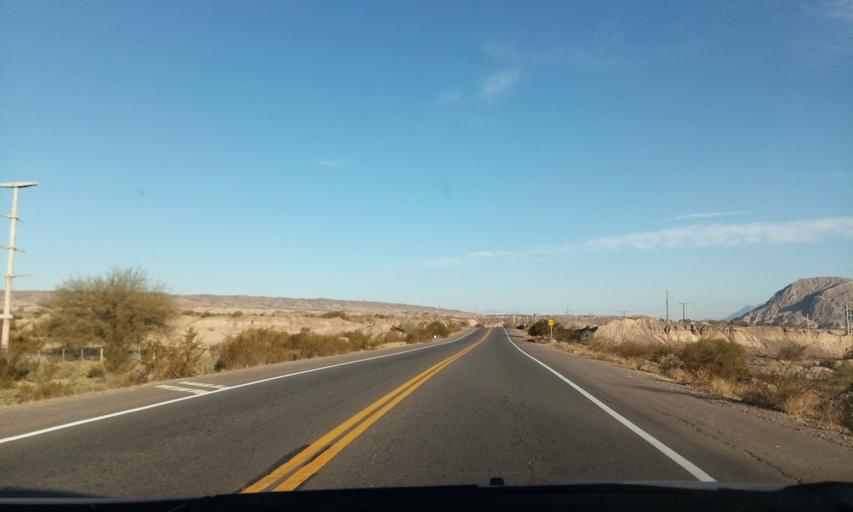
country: AR
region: San Juan
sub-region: Departamento de Rivadavia
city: Rivadavia
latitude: -31.4393
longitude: -68.6546
